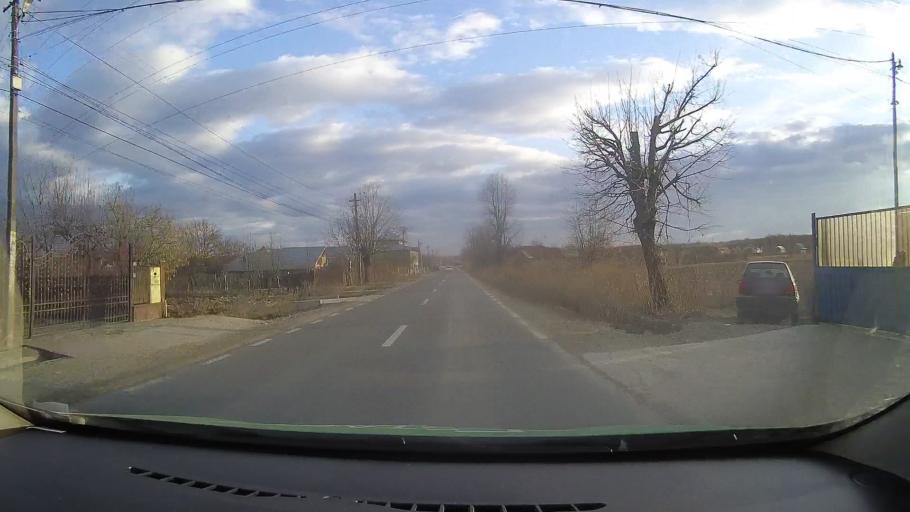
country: RO
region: Dambovita
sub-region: Comuna I. L. Caragiale
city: Ghirdoveni
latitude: 44.9569
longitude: 25.6575
